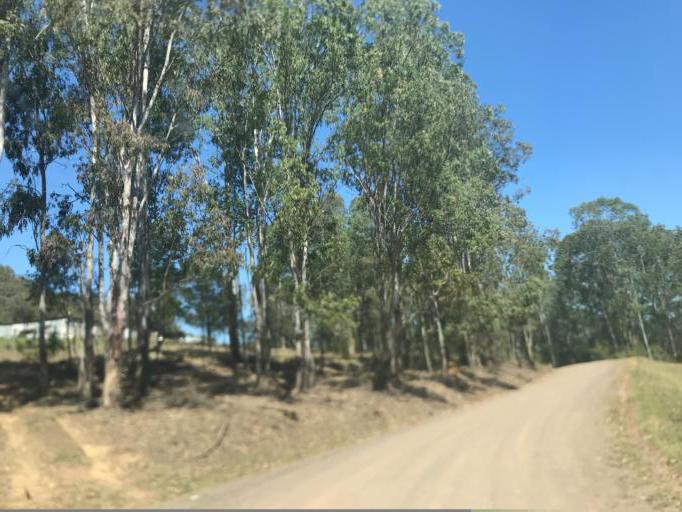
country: AU
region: New South Wales
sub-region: Hornsby Shire
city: Glenorie
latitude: -33.2554
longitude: 150.9757
